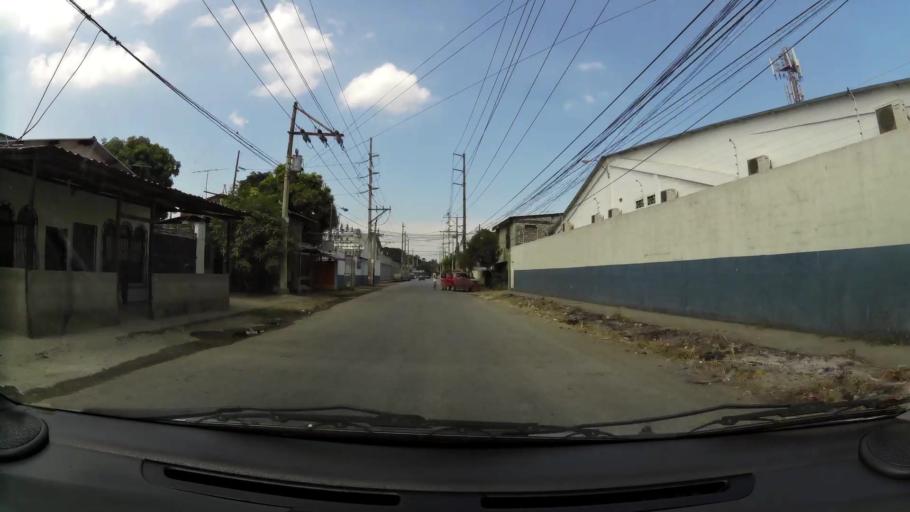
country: EC
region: Guayas
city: Guayaquil
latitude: -2.1369
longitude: -79.9365
